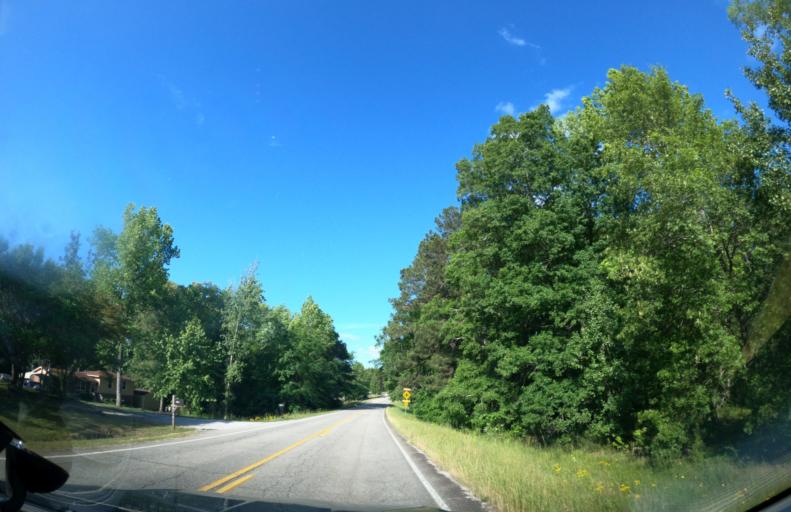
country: US
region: Georgia
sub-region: Columbia County
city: Harlem
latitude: 33.4343
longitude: -82.2833
